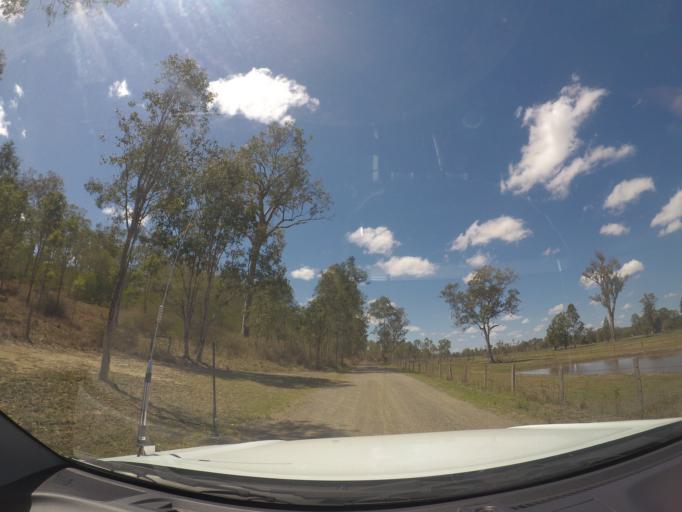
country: AU
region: Queensland
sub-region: Logan
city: Cedar Vale
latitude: -27.8511
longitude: 152.8958
